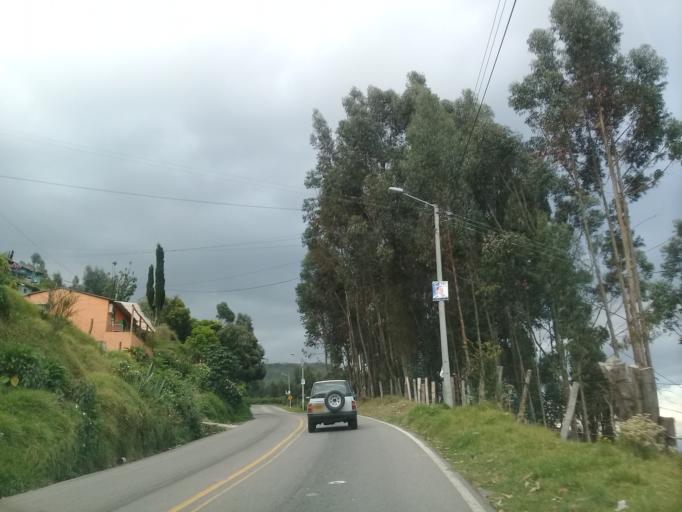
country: CO
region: Cundinamarca
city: Zipaquira
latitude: 5.0237
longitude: -74.0234
